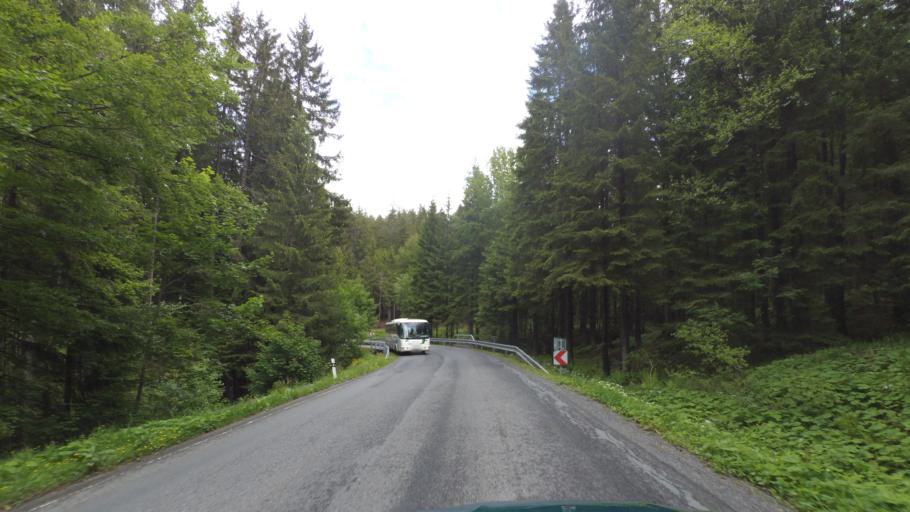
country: CZ
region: Plzensky
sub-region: Okres Klatovy
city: Zelezna Ruda
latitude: 49.1826
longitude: 13.2376
